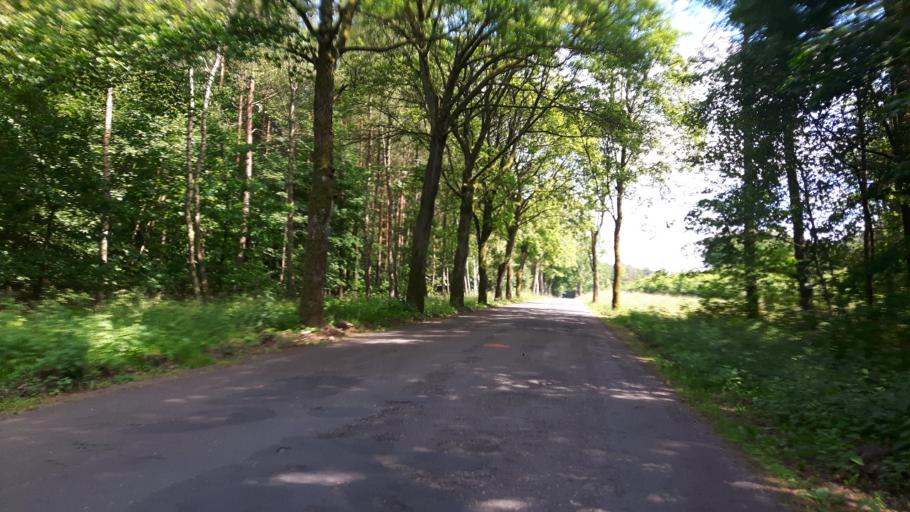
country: PL
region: West Pomeranian Voivodeship
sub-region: Powiat goleniowski
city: Osina
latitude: 53.6757
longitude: 15.0182
